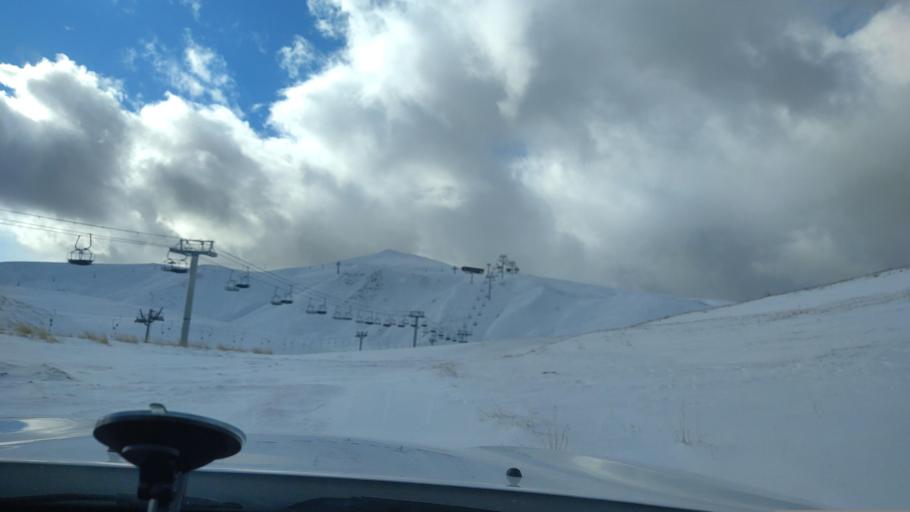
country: FR
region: Rhone-Alpes
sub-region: Departement de la Savoie
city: Saint-Etienne-de-Cuines
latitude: 45.2468
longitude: 6.2203
